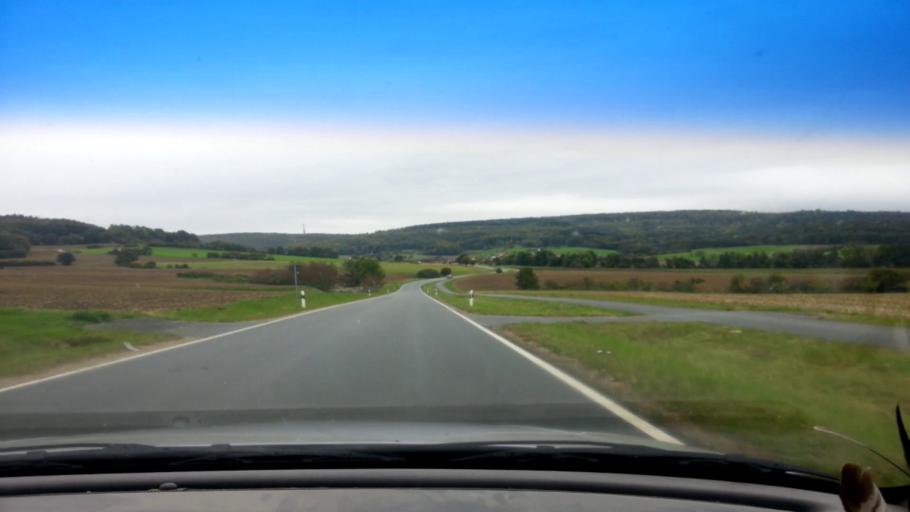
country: DE
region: Bavaria
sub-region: Upper Franconia
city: Litzendorf
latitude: 49.9074
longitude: 11.0167
